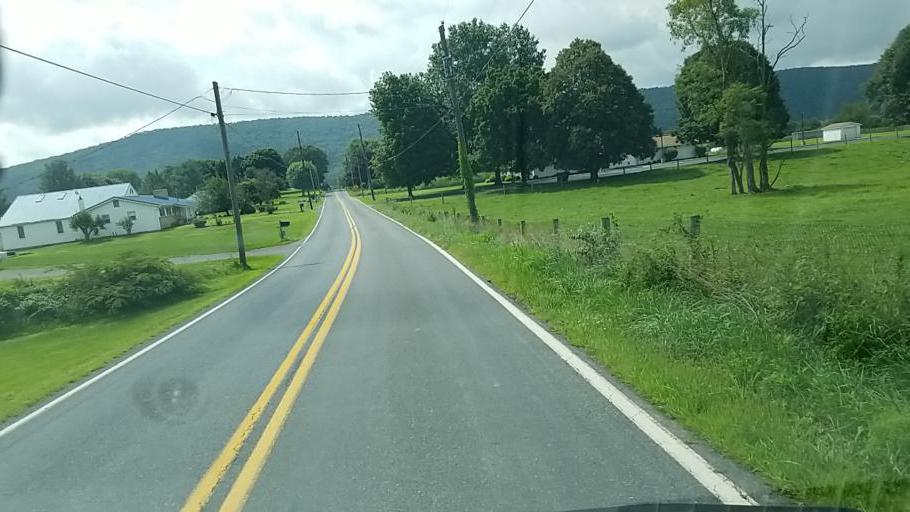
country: US
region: Pennsylvania
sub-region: Dauphin County
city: Millersburg
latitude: 40.5481
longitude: -76.8919
